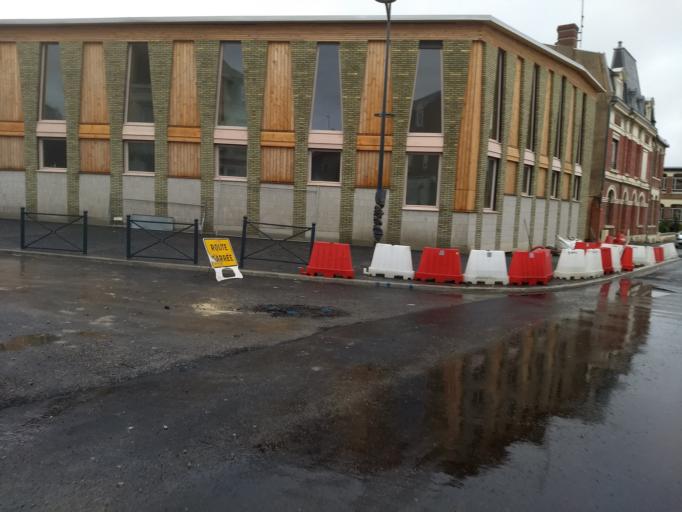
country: FR
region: Nord-Pas-de-Calais
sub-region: Departement du Pas-de-Calais
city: Arras
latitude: 50.2937
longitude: 2.7870
